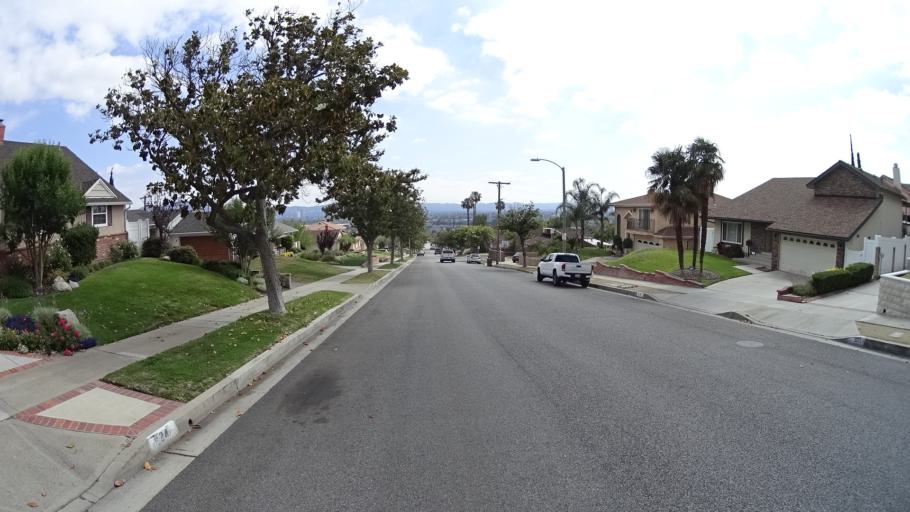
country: US
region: California
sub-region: Los Angeles County
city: Burbank
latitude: 34.2018
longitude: -118.3160
